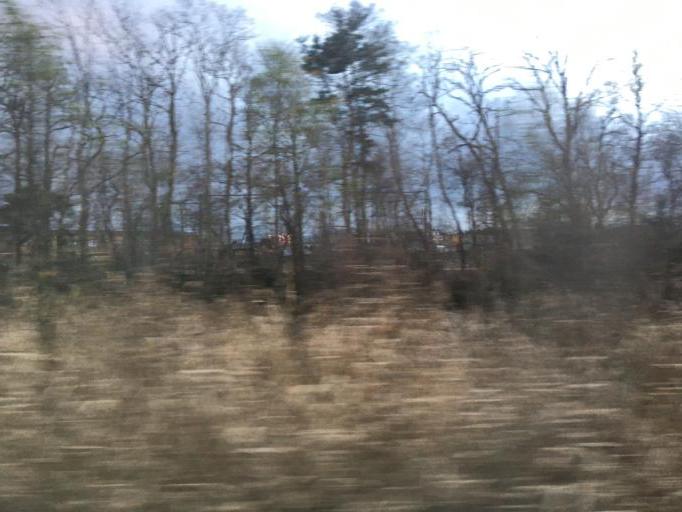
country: JP
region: Aomori
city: Aomori Shi
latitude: 40.8280
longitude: 140.6855
